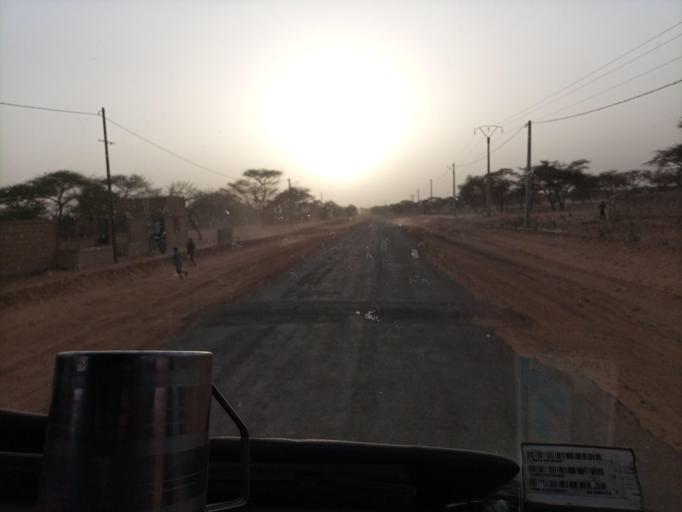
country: SN
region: Louga
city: Dara
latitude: 15.4014
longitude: -15.6565
